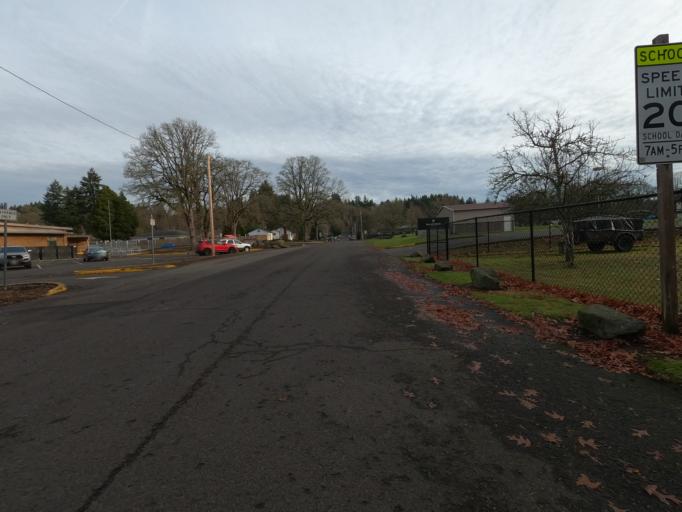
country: US
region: Oregon
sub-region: Clackamas County
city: Jennings Lodge
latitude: 45.3922
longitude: -122.6024
